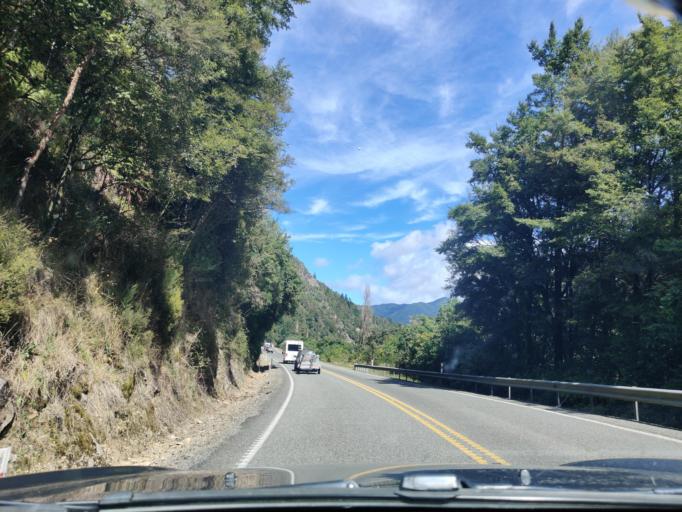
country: NZ
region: West Coast
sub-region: Buller District
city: Westport
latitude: -41.7691
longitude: 172.2307
